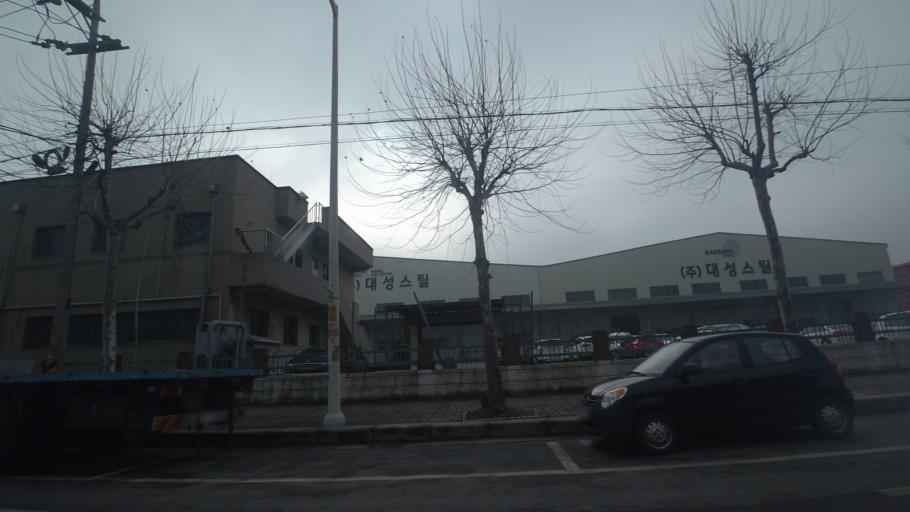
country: KR
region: Gyeonggi-do
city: Hwaseong-si
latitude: 36.9881
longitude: 126.8519
